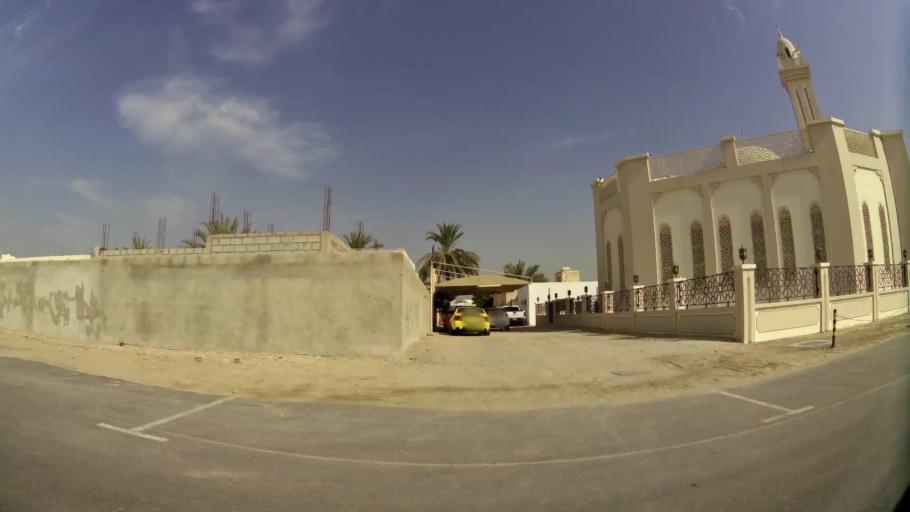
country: AE
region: Ash Shariqah
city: Sharjah
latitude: 25.2636
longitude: 55.3945
